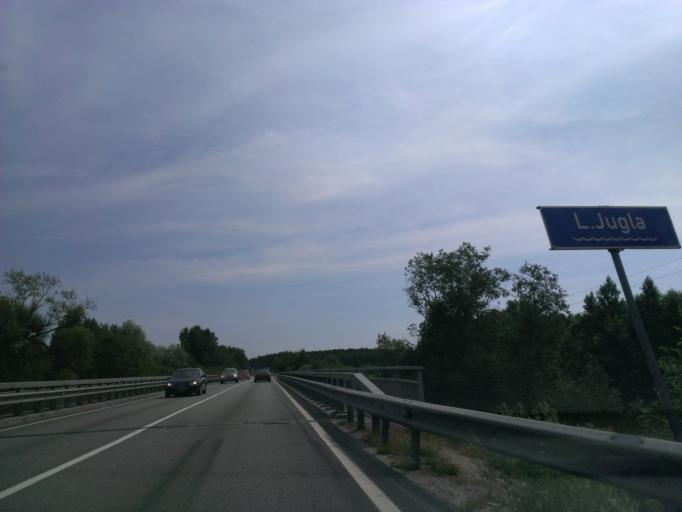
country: LV
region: Riga
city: Bergi
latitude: 56.9775
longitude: 24.3342
